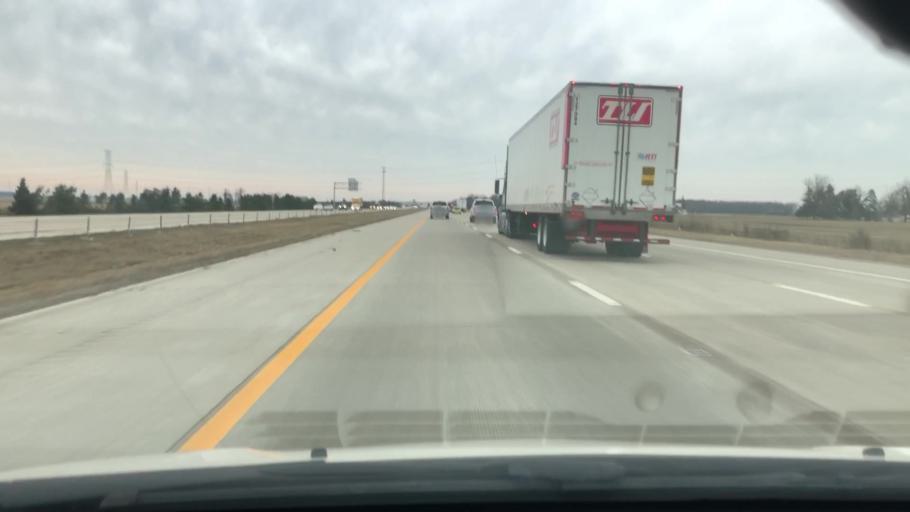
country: US
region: Ohio
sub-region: Wood County
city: Haskins
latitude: 41.4685
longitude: -83.6221
